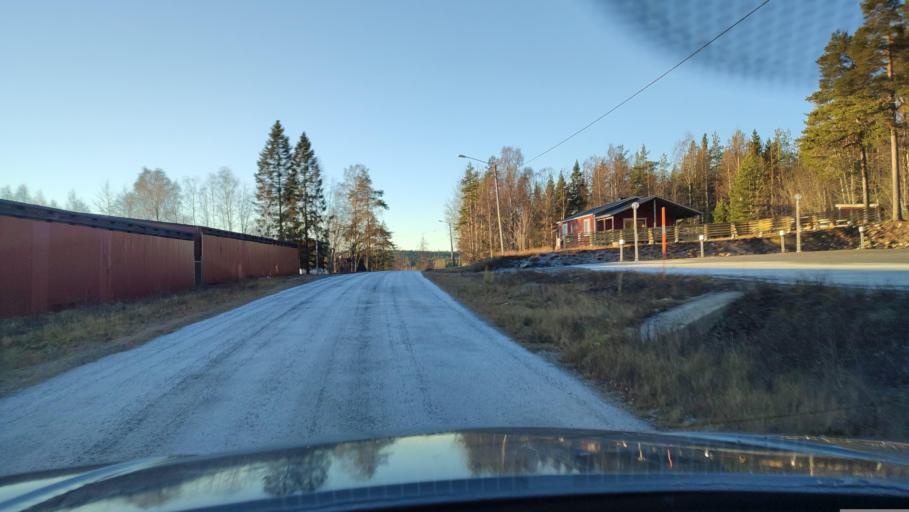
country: SE
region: Vaesterbotten
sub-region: Skelleftea Kommun
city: Viken
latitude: 64.7031
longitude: 20.9032
